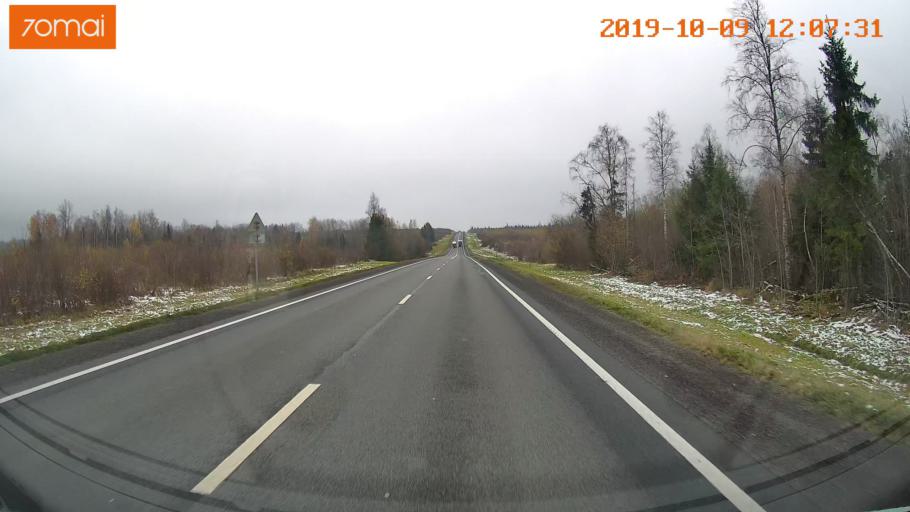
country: RU
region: Jaroslavl
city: Prechistoye
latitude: 58.5982
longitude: 40.3424
